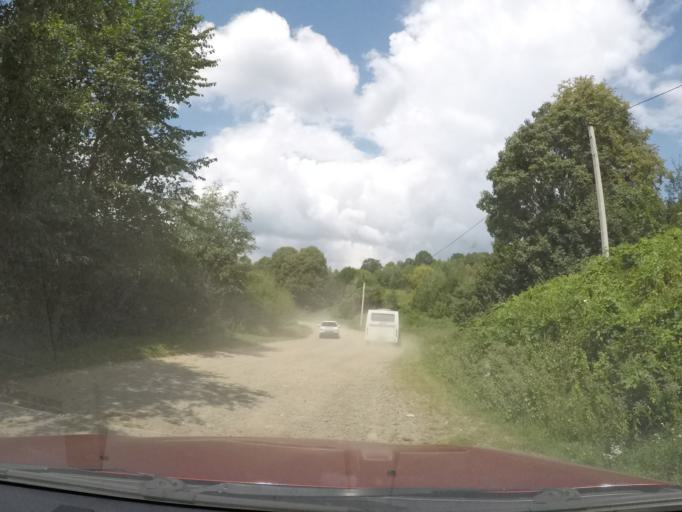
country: UA
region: Zakarpattia
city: Velykyi Bereznyi
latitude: 49.0279
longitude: 22.5951
